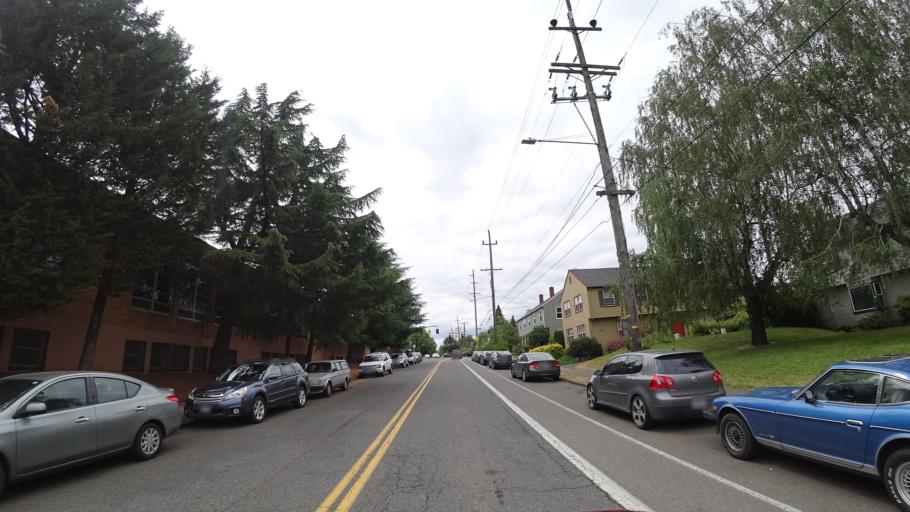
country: US
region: Oregon
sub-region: Multnomah County
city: Portland
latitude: 45.5708
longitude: -122.6689
